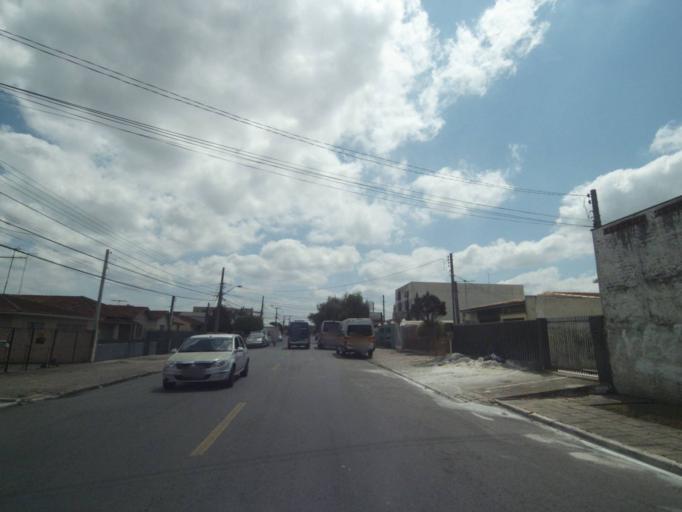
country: BR
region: Parana
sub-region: Curitiba
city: Curitiba
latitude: -25.5024
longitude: -49.2980
